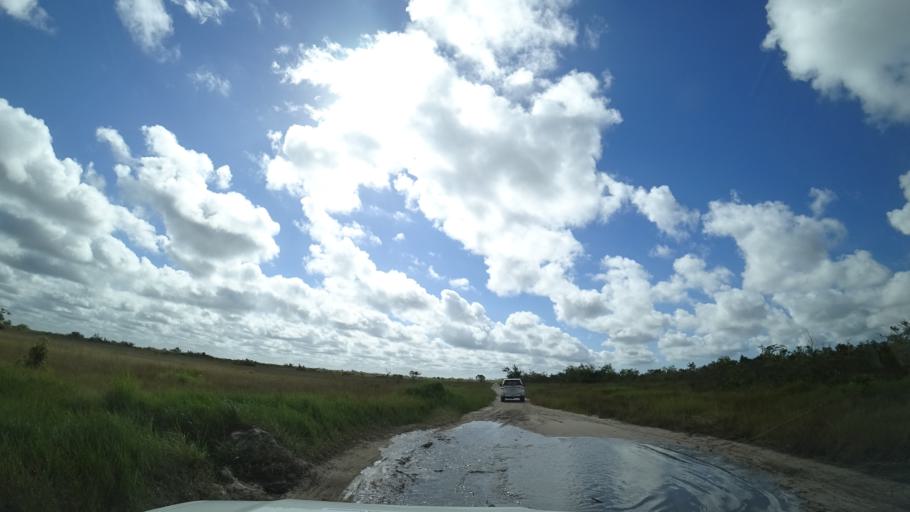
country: MZ
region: Sofala
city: Beira
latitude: -19.6165
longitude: 35.0615
